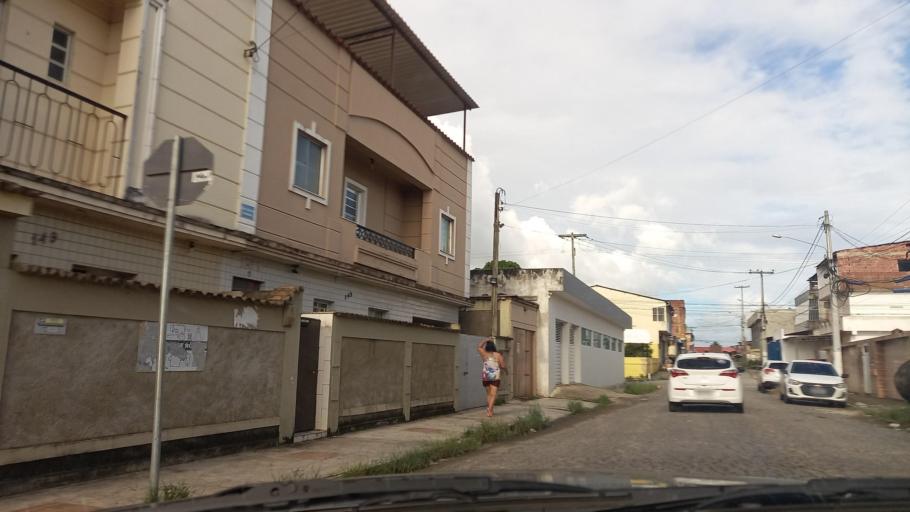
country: BR
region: Pernambuco
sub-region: Palmares
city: Palmares
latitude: -8.6756
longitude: -35.5791
